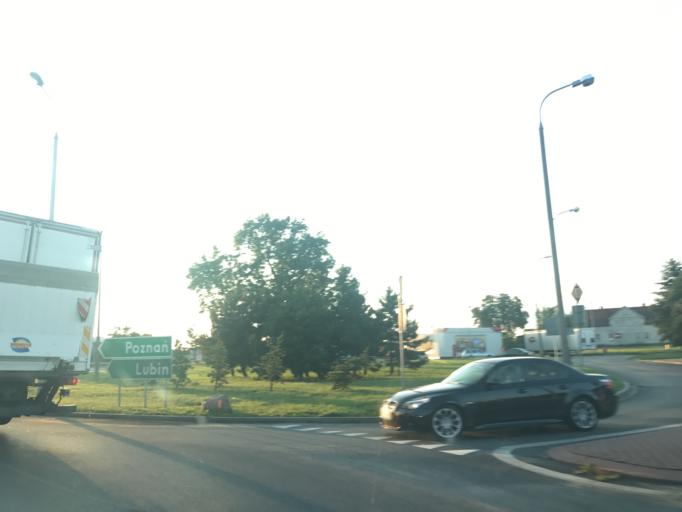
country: PL
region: Greater Poland Voivodeship
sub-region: Powiat rawicki
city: Rawicz
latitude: 51.6177
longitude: 16.8599
